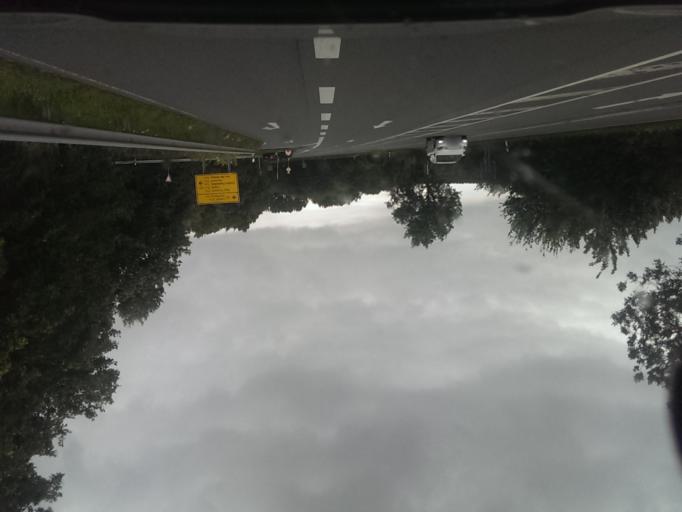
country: DE
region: North Rhine-Westphalia
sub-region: Regierungsbezirk Detmold
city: Steinheim
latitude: 51.8973
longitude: 9.0863
